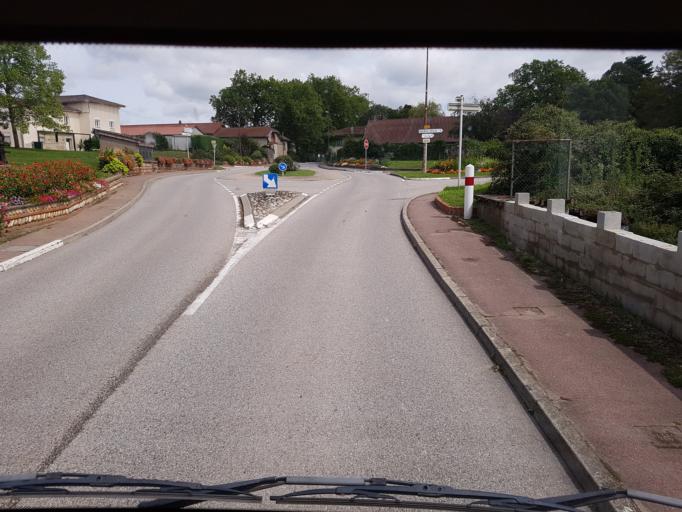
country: FR
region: Rhone-Alpes
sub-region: Departement de l'Ain
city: Dagneux
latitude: 45.9301
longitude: 5.0725
